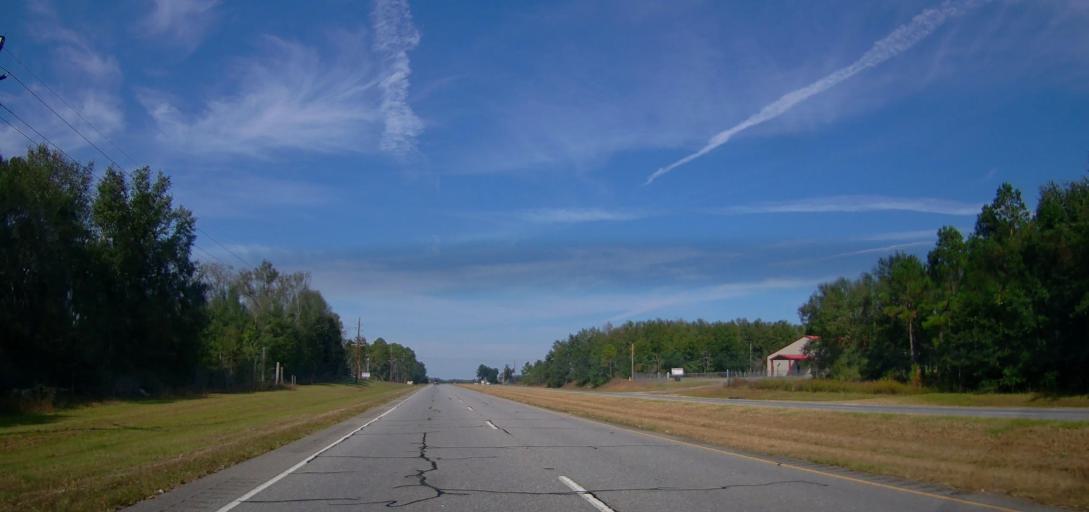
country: US
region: Georgia
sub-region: Mitchell County
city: Camilla
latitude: 31.3204
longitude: -84.1738
